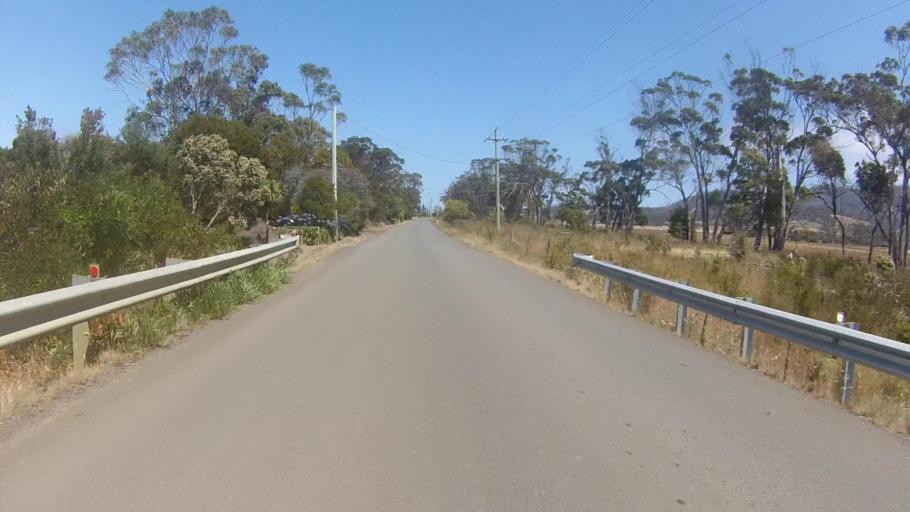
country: AU
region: Tasmania
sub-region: Sorell
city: Sorell
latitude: -42.8586
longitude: 147.8357
